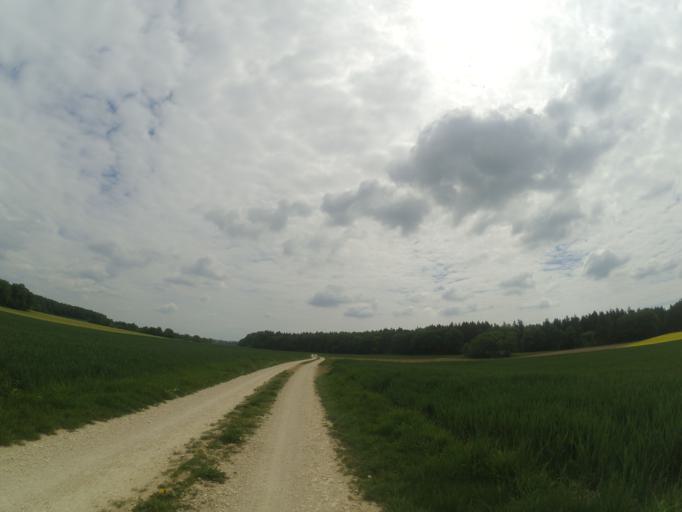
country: DE
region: Baden-Wuerttemberg
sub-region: Tuebingen Region
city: Blaubeuren
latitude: 48.4254
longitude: 9.8326
